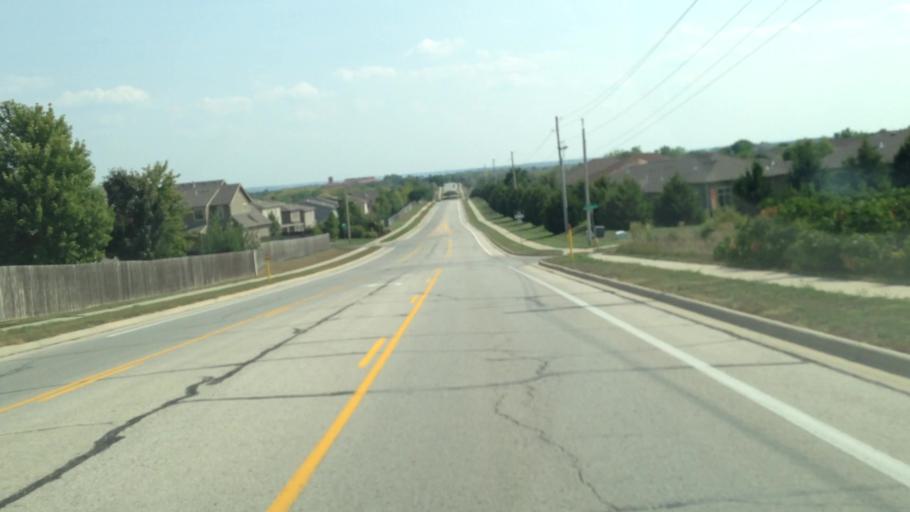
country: US
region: Kansas
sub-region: Douglas County
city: Lawrence
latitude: 38.9698
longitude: -95.3258
